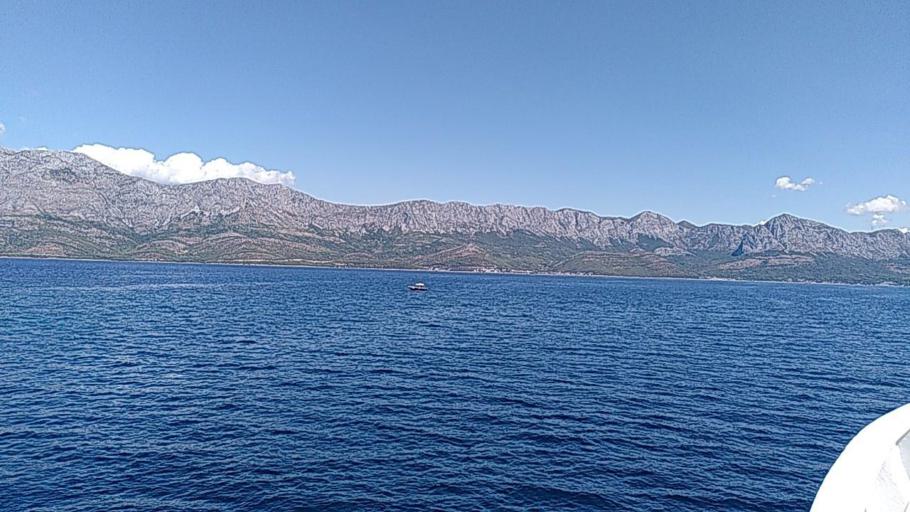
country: HR
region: Dubrovacko-Neretvanska
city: Orebic
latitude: 43.1235
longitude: 17.1969
